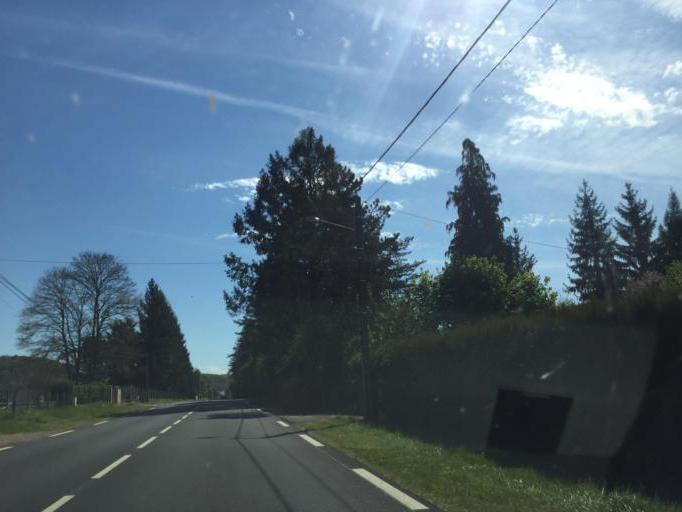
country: FR
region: Bourgogne
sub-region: Departement de la Nievre
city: Clamecy
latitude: 47.4360
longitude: 3.5750
